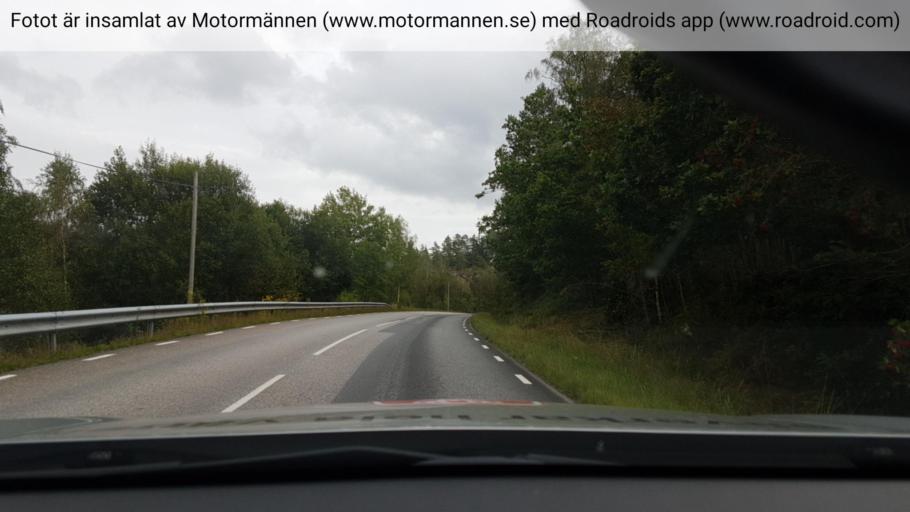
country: SE
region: Vaestra Goetaland
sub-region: Sotenas Kommun
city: Hunnebostrand
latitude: 58.5601
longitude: 11.3995
